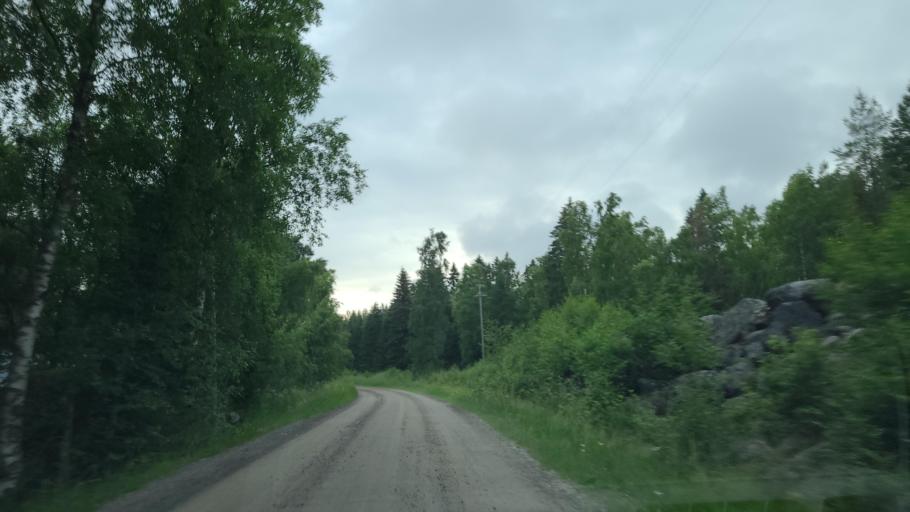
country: FI
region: Ostrobothnia
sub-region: Vaasa
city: Replot
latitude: 63.3152
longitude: 21.1585
